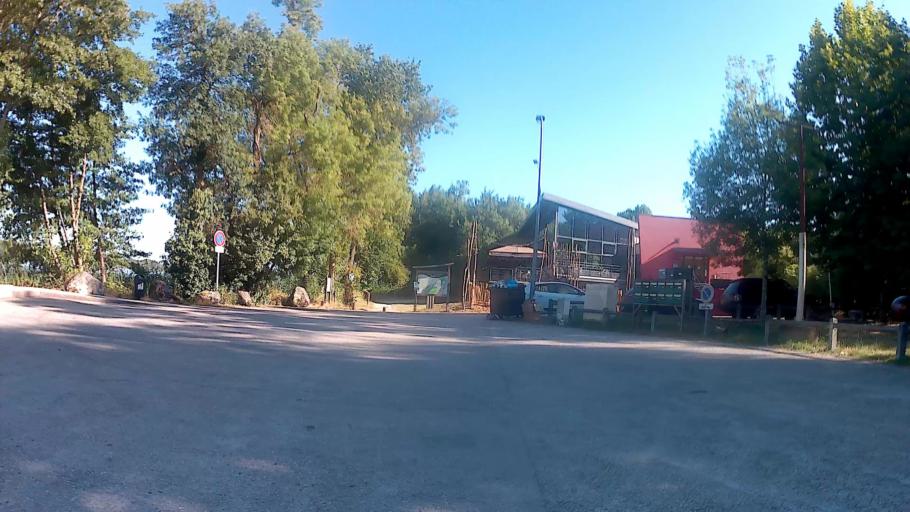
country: FR
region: Aquitaine
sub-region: Departement de la Gironde
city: Begles
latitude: 44.7977
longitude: -0.5286
